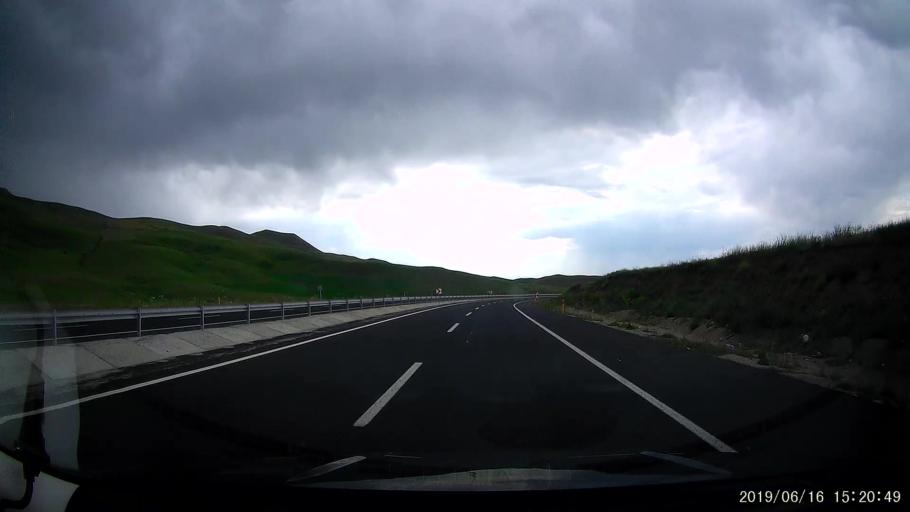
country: TR
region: Erzurum
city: Aras
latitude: 39.9729
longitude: 42.2562
